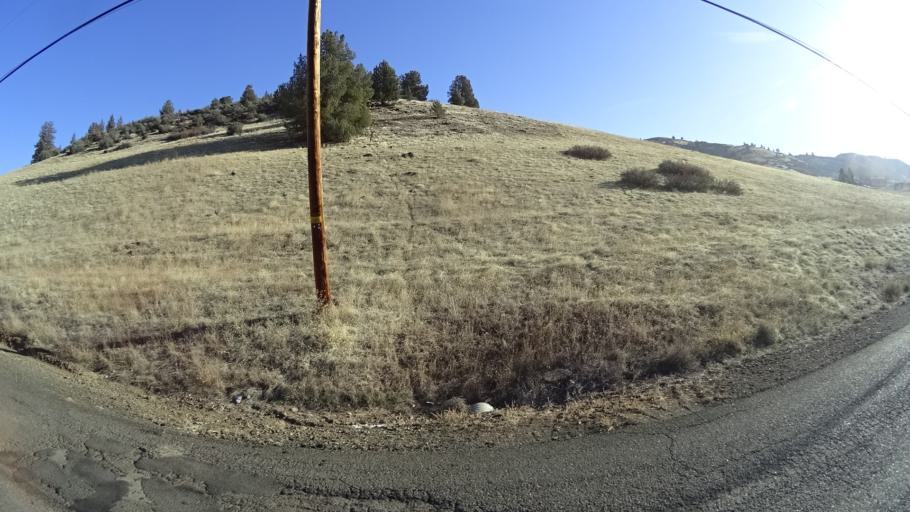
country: US
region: California
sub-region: Siskiyou County
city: Montague
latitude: 41.8897
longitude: -122.4805
